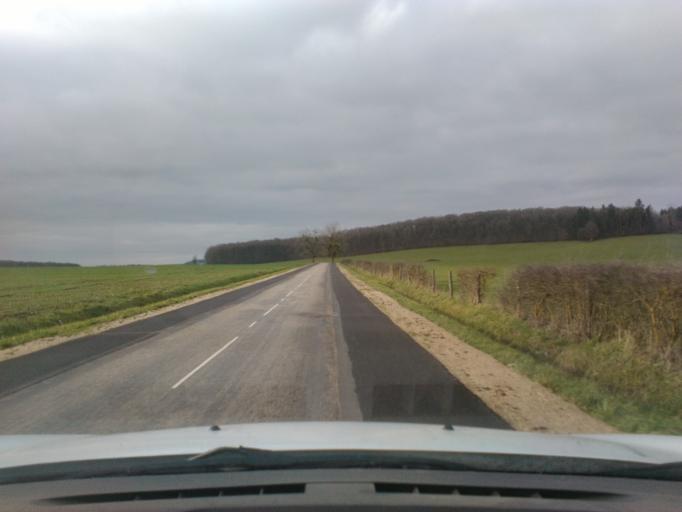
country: FR
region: Lorraine
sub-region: Departement des Vosges
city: Mirecourt
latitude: 48.3362
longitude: 6.0108
